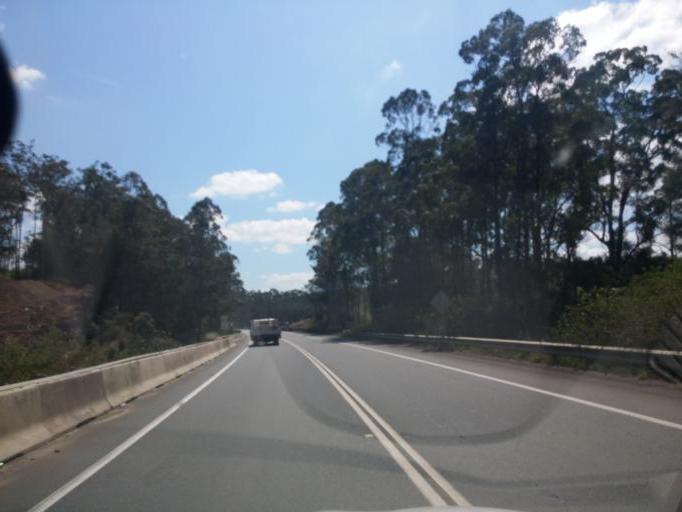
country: AU
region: New South Wales
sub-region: Port Macquarie-Hastings
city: North Shore
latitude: -31.3052
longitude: 152.8212
